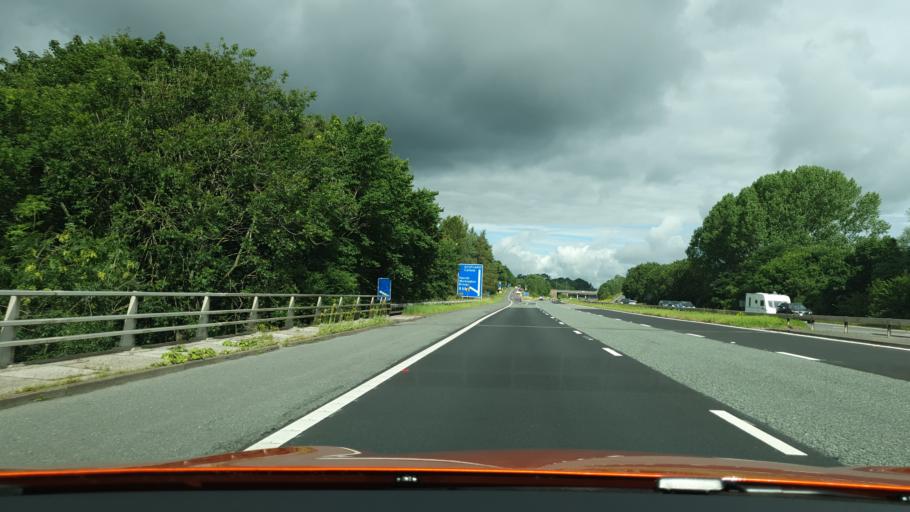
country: GB
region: England
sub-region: Cumbria
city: Penrith
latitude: 54.6489
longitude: -2.7515
